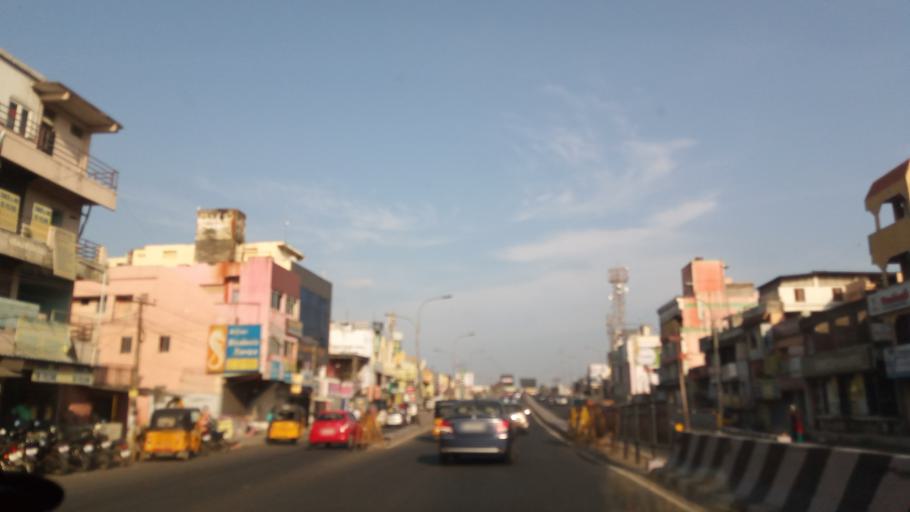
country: IN
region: Tamil Nadu
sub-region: Thiruvallur
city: Porur
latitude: 13.0360
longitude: 80.1536
